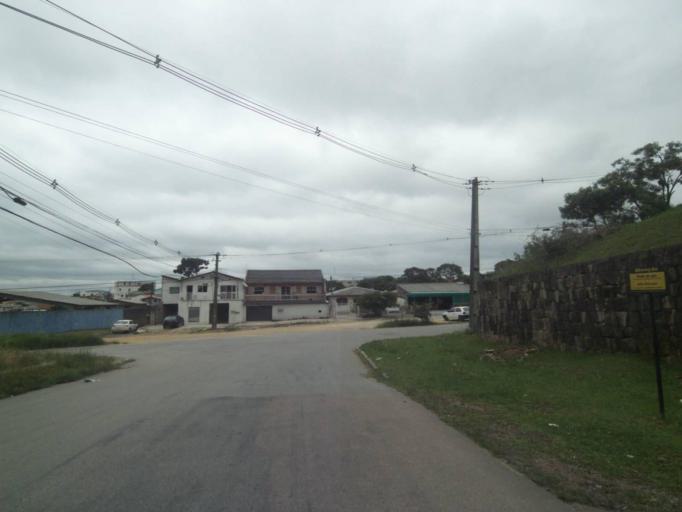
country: BR
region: Parana
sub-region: Araucaria
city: Araucaria
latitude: -25.5598
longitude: -49.3110
